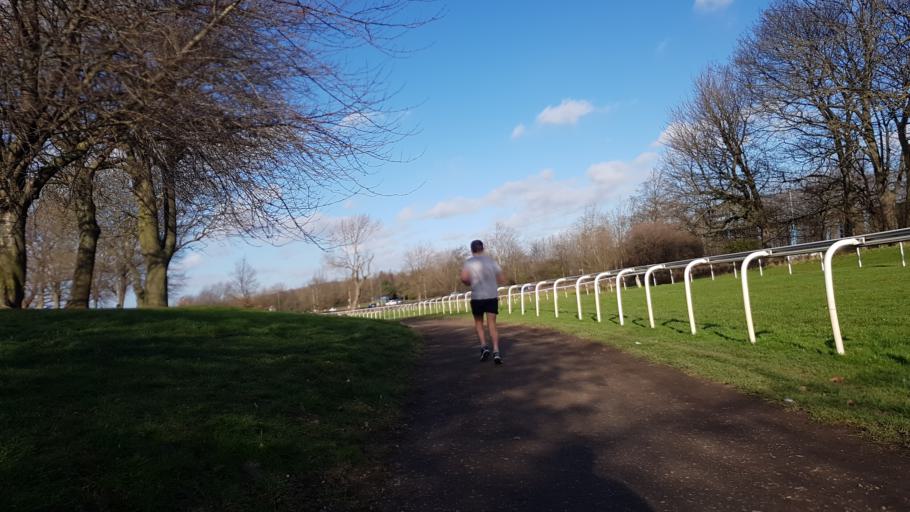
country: GB
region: England
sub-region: City and Borough of Wakefield
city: Pontefract
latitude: 53.6984
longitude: -1.3251
